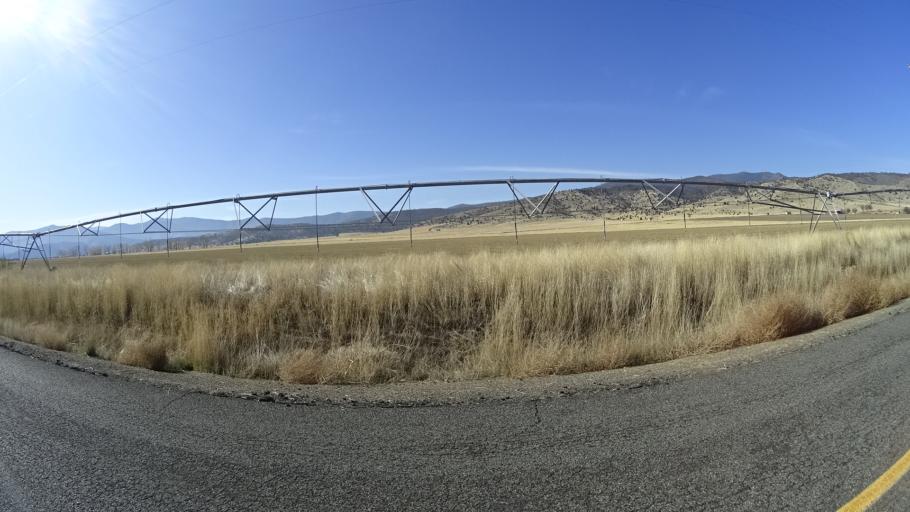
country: US
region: California
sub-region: Siskiyou County
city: Montague
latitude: 41.5648
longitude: -122.5481
